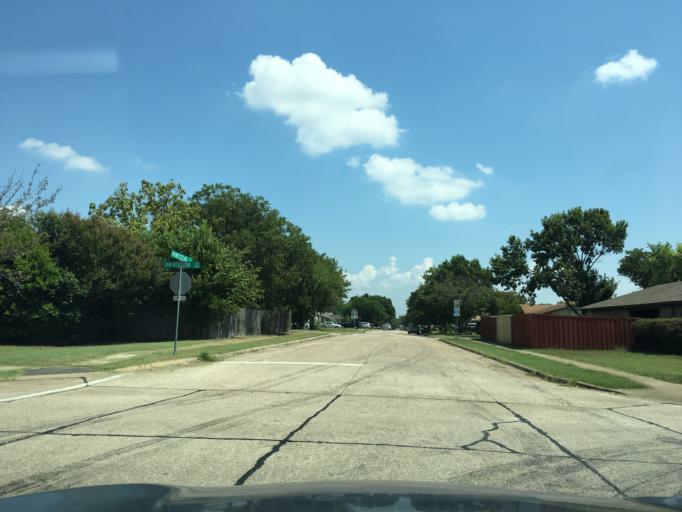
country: US
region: Texas
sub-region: Dallas County
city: Garland
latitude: 32.9382
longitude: -96.6572
